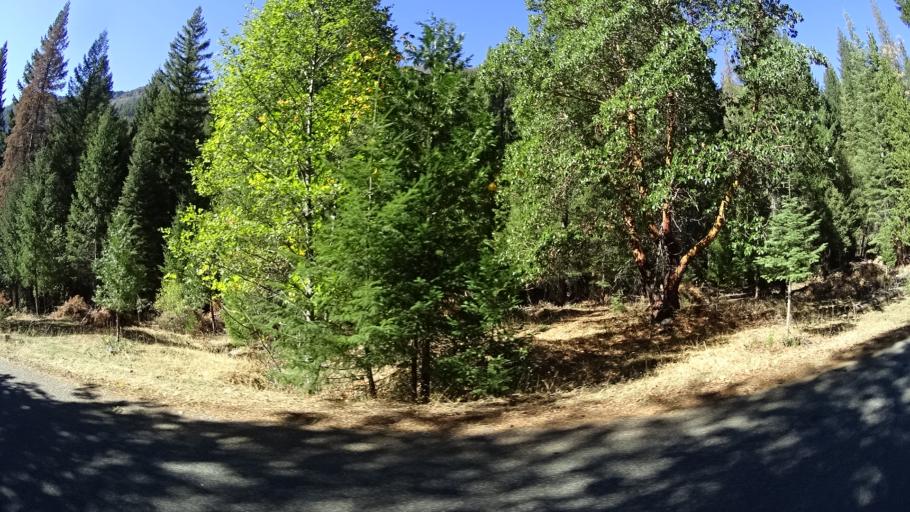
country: US
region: California
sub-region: Siskiyou County
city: Yreka
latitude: 41.3723
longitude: -123.0218
